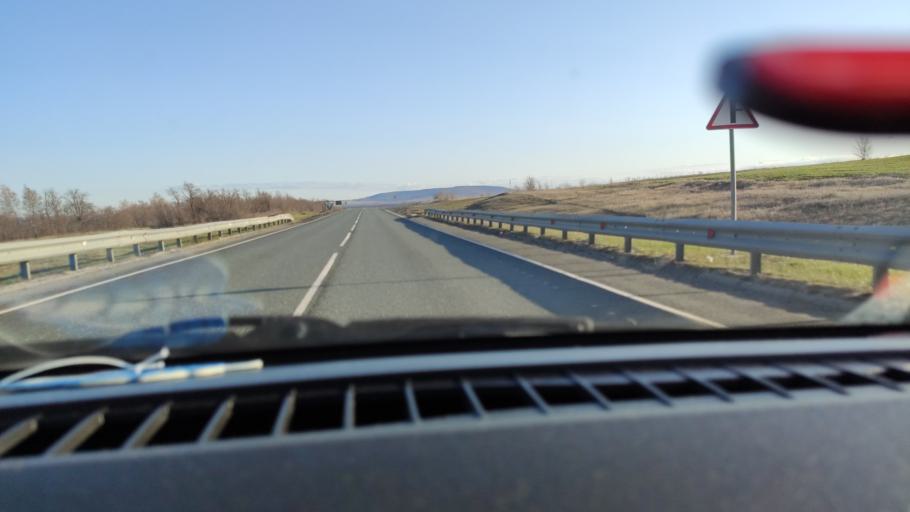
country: RU
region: Saratov
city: Alekseyevka
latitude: 52.2305
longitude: 47.9029
